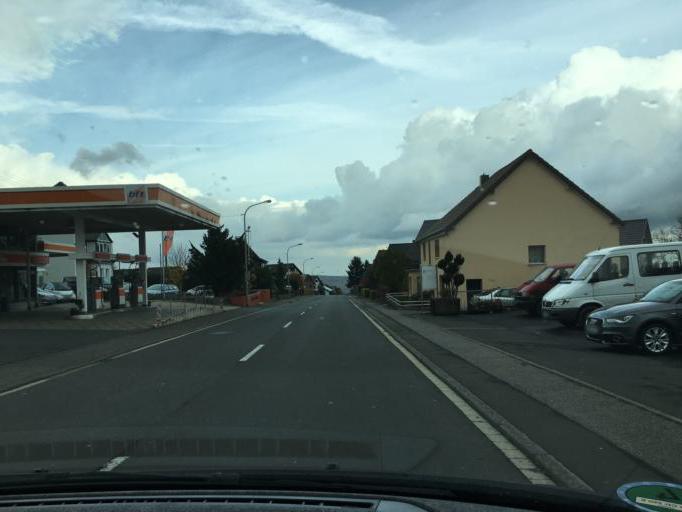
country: DE
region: North Rhine-Westphalia
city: Heimbach
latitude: 50.6613
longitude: 6.4123
